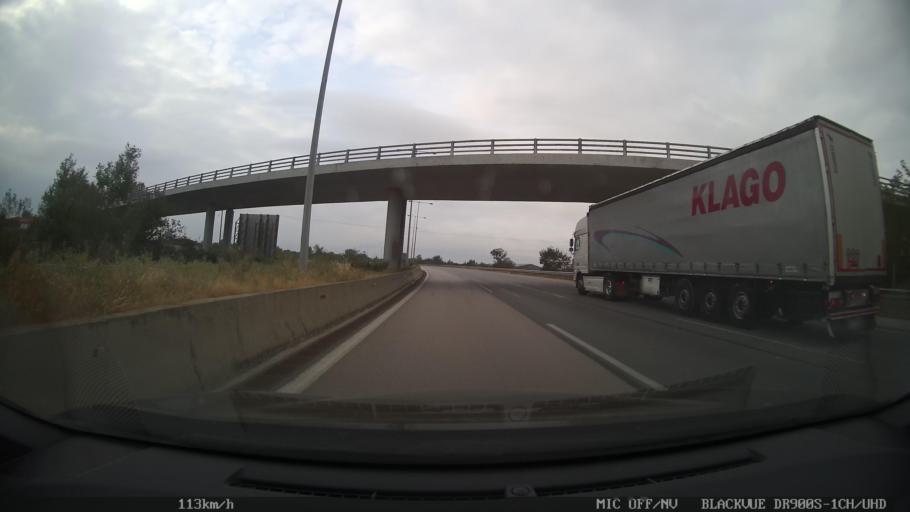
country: GR
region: Central Macedonia
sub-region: Nomos Thessalonikis
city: Nea Magnisia
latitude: 40.6891
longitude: 22.8357
